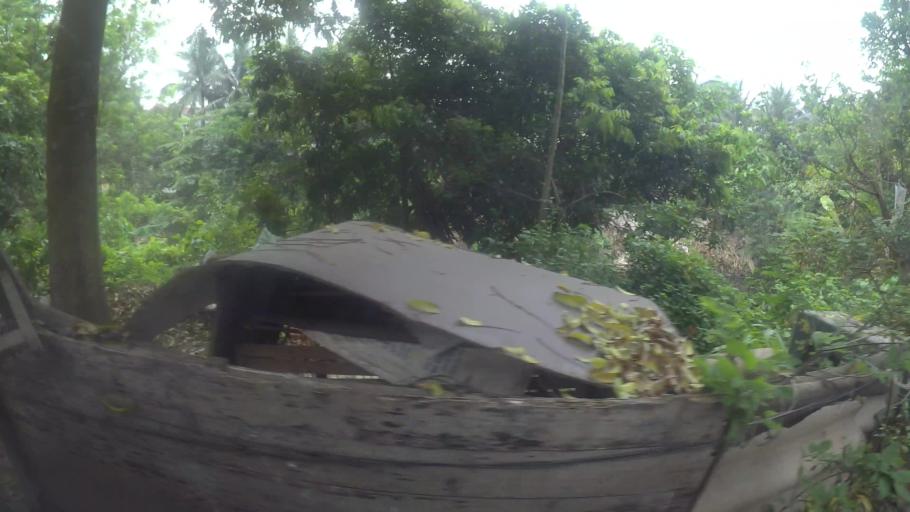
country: VN
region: Ha Noi
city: Ha Dong
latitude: 20.9709
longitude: 105.7581
